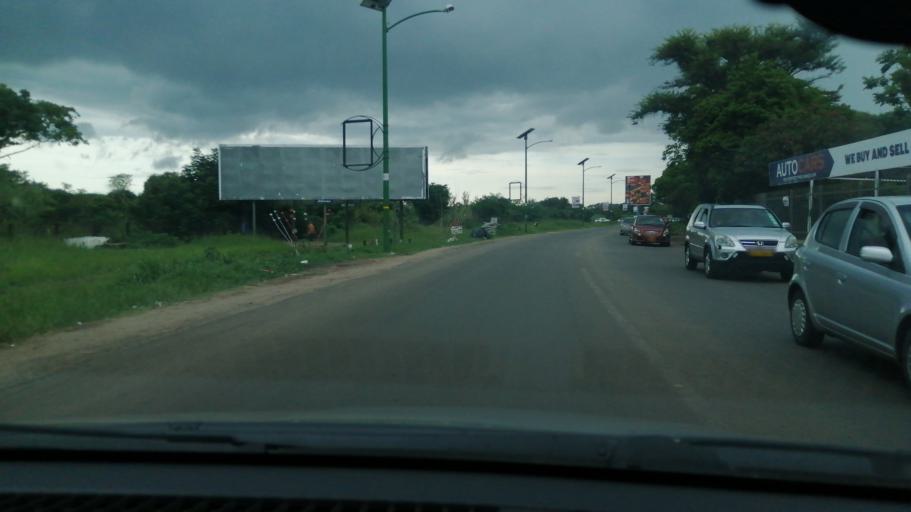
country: ZW
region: Harare
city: Harare
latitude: -17.7909
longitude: 31.0457
